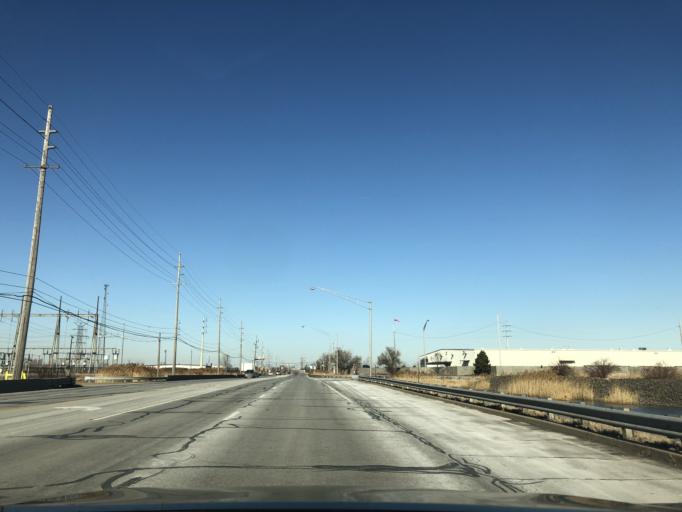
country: US
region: Indiana
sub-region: Lake County
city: Whiting
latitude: 41.6573
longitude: -87.5085
